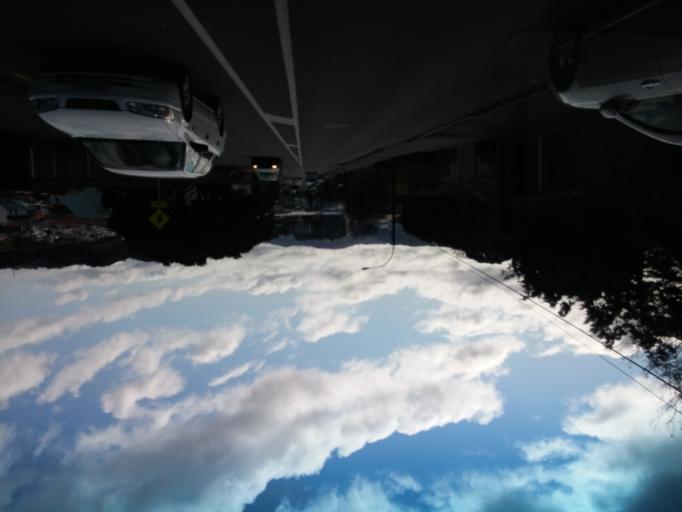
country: NZ
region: Wellington
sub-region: Wellington City
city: Brooklyn
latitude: -41.3186
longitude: 174.7805
